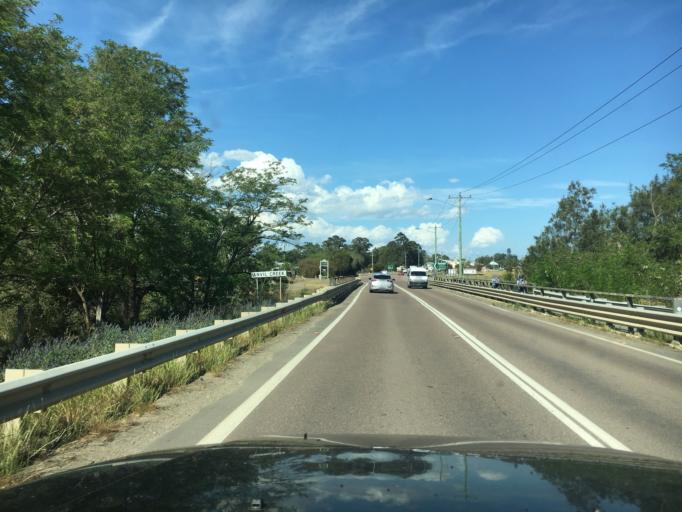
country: AU
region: New South Wales
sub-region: Cessnock
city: Branxton
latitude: -32.6560
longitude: 151.3558
